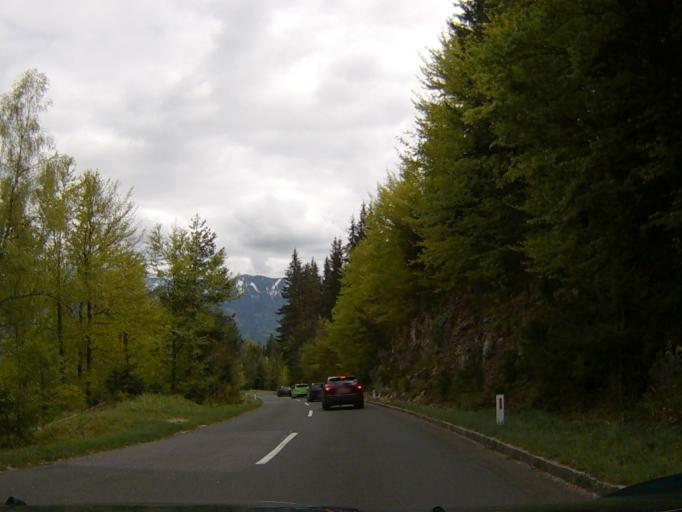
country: AT
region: Carinthia
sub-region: Politischer Bezirk Villach Land
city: Arnoldstein
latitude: 46.5861
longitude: 13.7782
